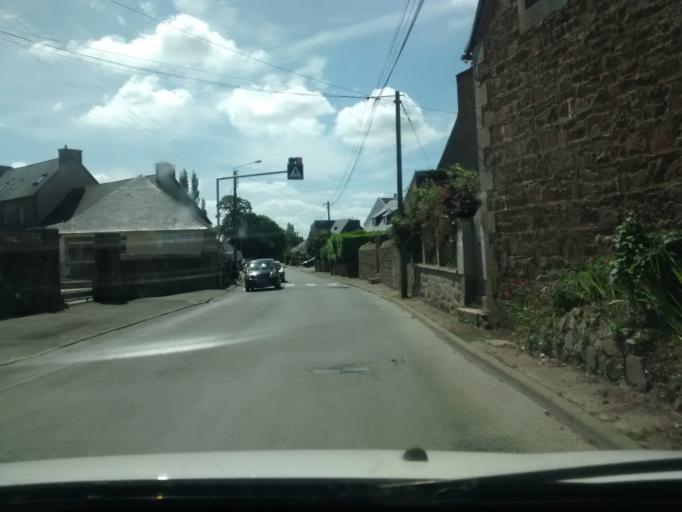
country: FR
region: Brittany
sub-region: Departement des Cotes-d'Armor
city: Penvenan
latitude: 48.8151
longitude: -3.2970
